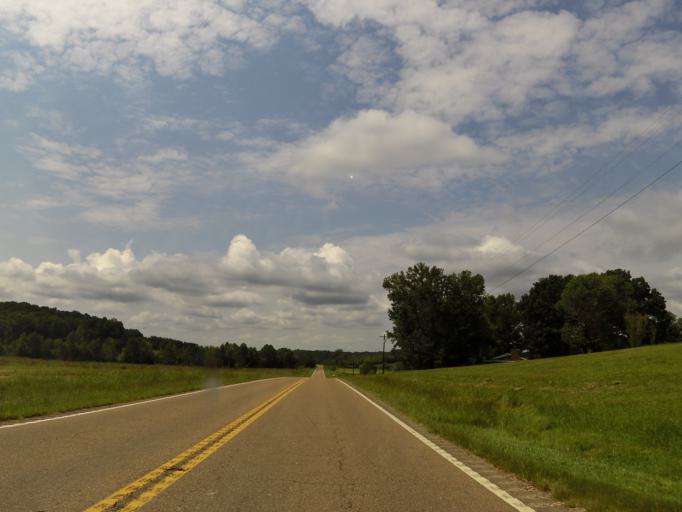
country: US
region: Tennessee
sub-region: Henderson County
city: Lexington
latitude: 35.5011
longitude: -88.3610
